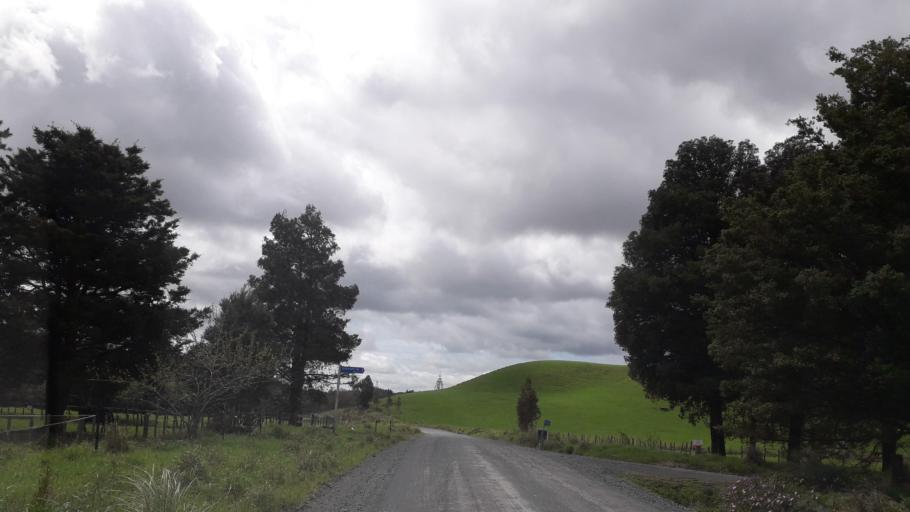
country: NZ
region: Northland
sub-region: Far North District
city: Kaitaia
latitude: -35.1736
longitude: 173.3286
